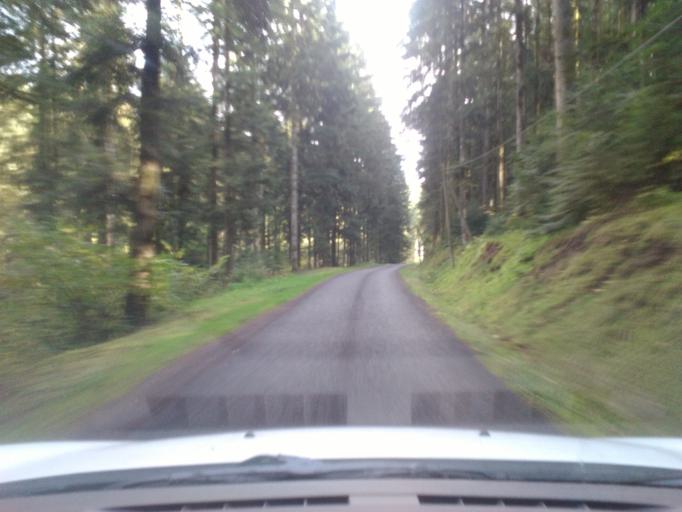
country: FR
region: Lorraine
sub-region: Departement des Vosges
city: Ban-de-Laveline
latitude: 48.3000
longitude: 7.0514
